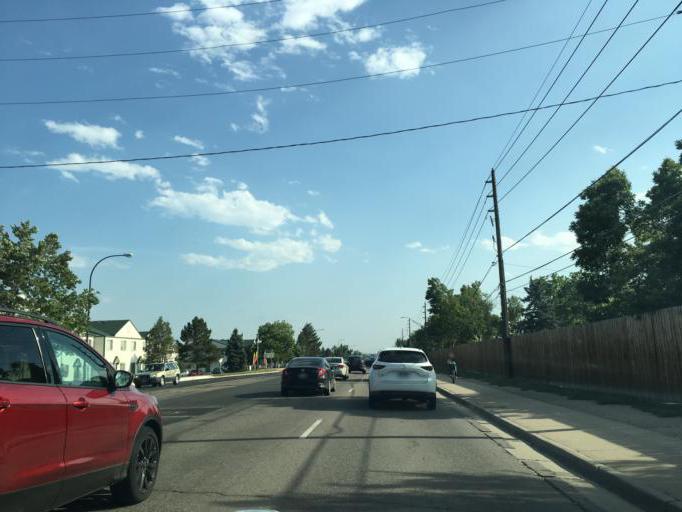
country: US
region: Colorado
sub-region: Adams County
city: Westminster
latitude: 39.8491
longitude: -105.0533
